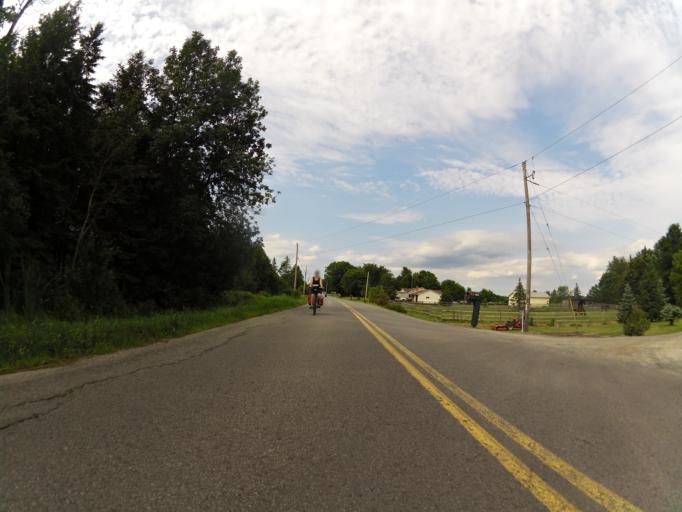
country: CA
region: Ontario
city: Prescott
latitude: 45.0391
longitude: -75.6191
